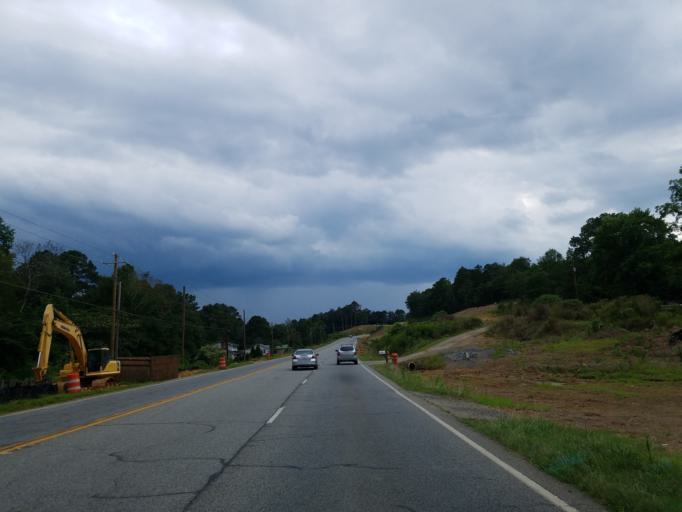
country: US
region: Georgia
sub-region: Bartow County
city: Adairsville
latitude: 34.3710
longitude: -84.9706
